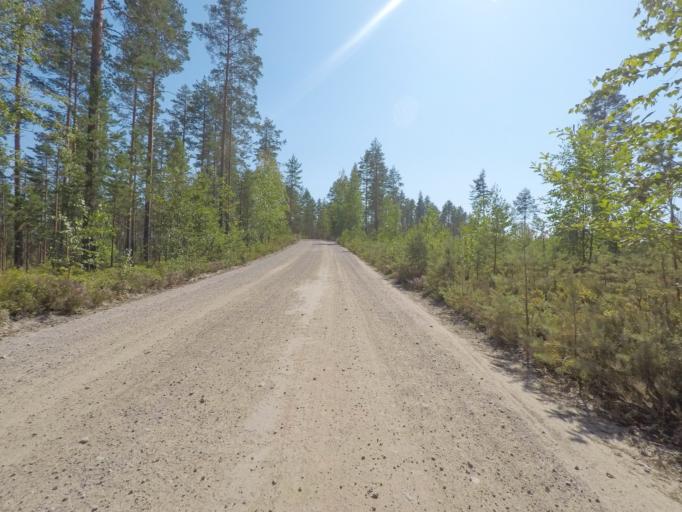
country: FI
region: Southern Savonia
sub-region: Mikkeli
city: Puumala
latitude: 61.4209
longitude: 28.0422
